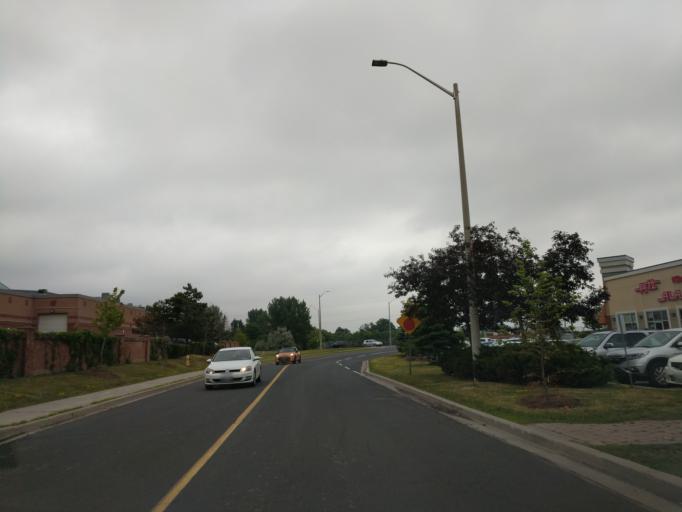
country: CA
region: Ontario
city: Markham
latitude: 43.8480
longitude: -79.3488
